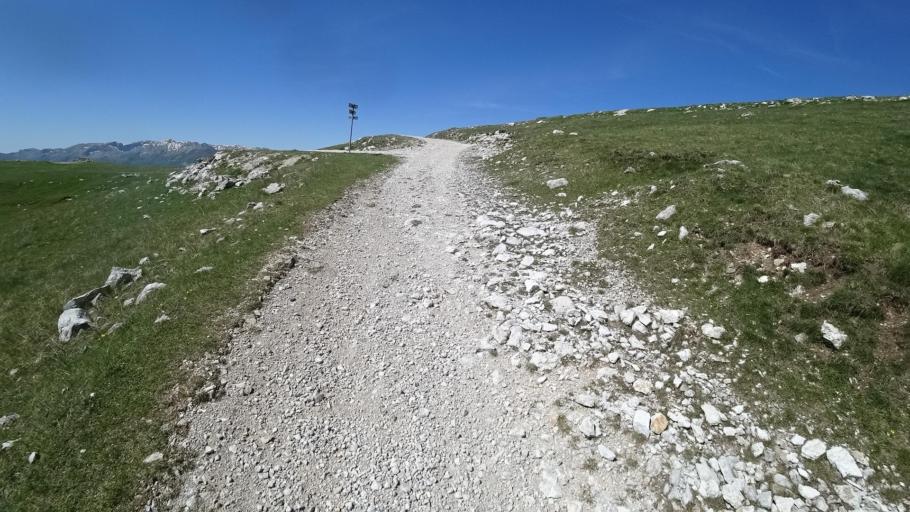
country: BA
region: Federation of Bosnia and Herzegovina
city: Gracanica
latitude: 43.6942
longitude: 18.2678
